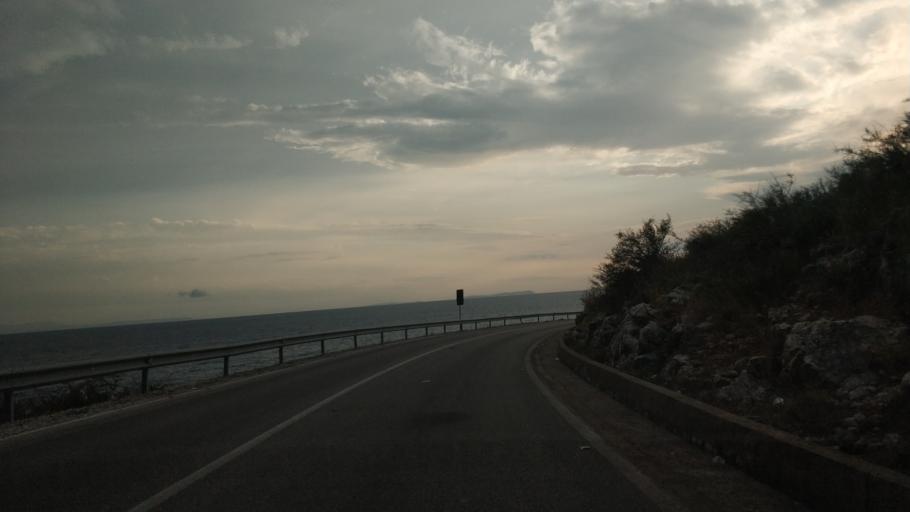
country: AL
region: Vlore
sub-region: Rrethi i Vlores
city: Himare
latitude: 40.0474
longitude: 19.8109
